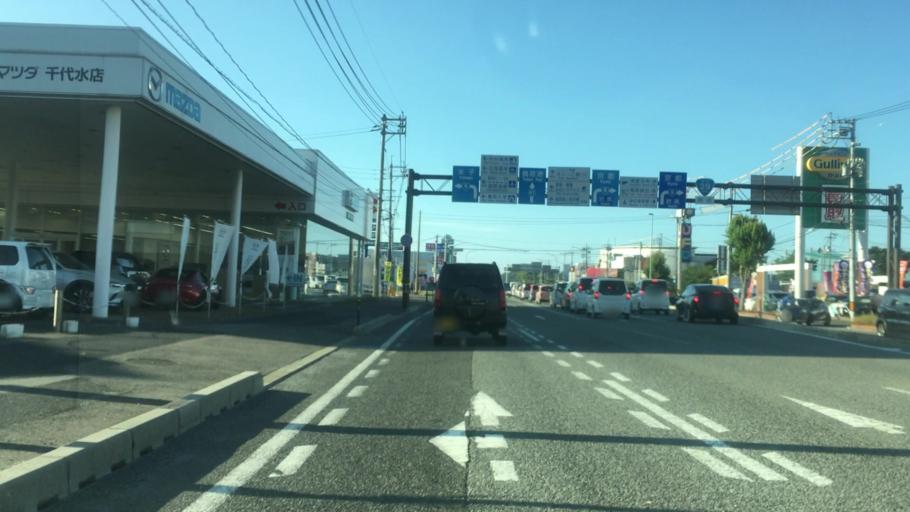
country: JP
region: Tottori
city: Tottori
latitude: 35.5181
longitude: 134.2022
